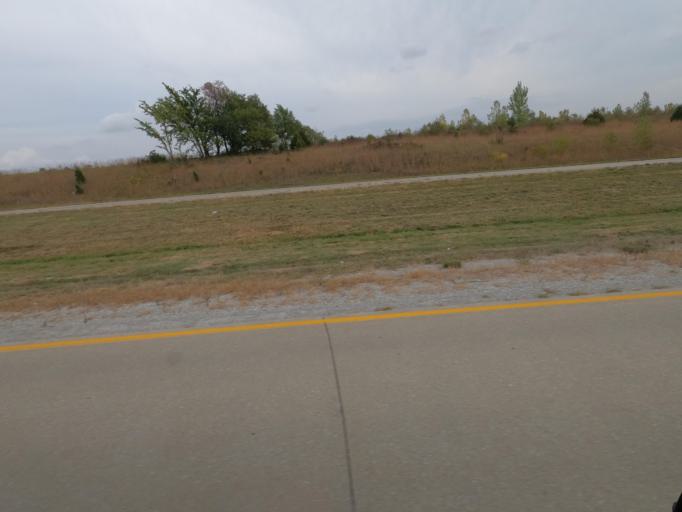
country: US
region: Iowa
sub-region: Jasper County
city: Monroe
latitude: 41.5187
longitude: -93.1303
